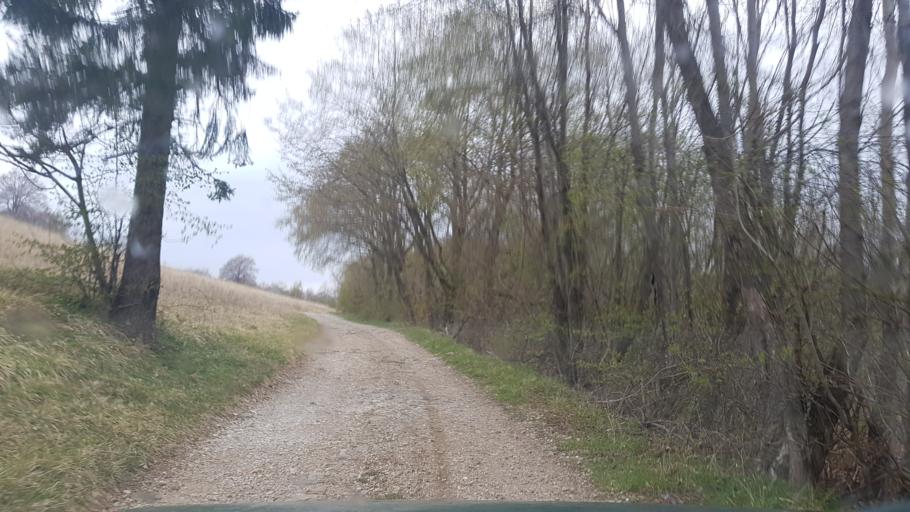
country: SI
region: Kanal
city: Deskle
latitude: 46.0671
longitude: 13.5625
